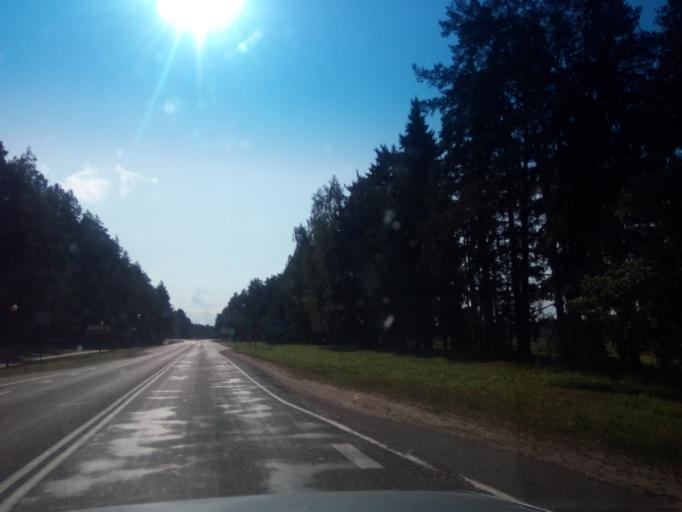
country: BY
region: Vitebsk
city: Vyerkhnyadzvinsk
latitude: 55.7567
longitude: 27.9535
